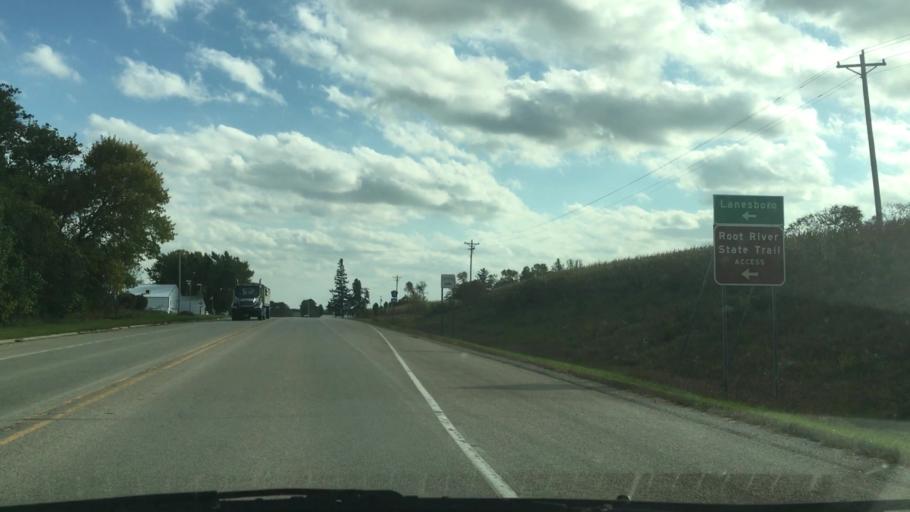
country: US
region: Minnesota
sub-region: Fillmore County
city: Preston
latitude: 43.7391
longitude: -92.1393
